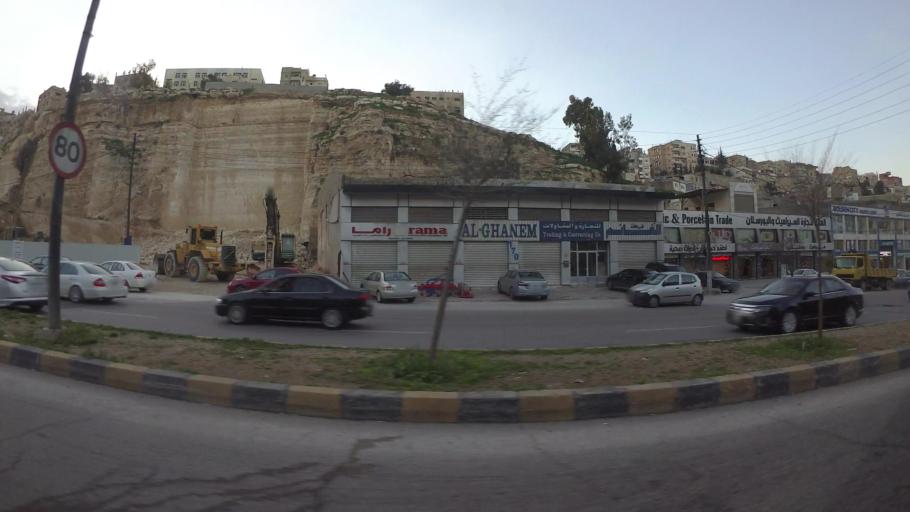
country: JO
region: Amman
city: Al Quwaysimah
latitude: 31.9306
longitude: 35.9211
